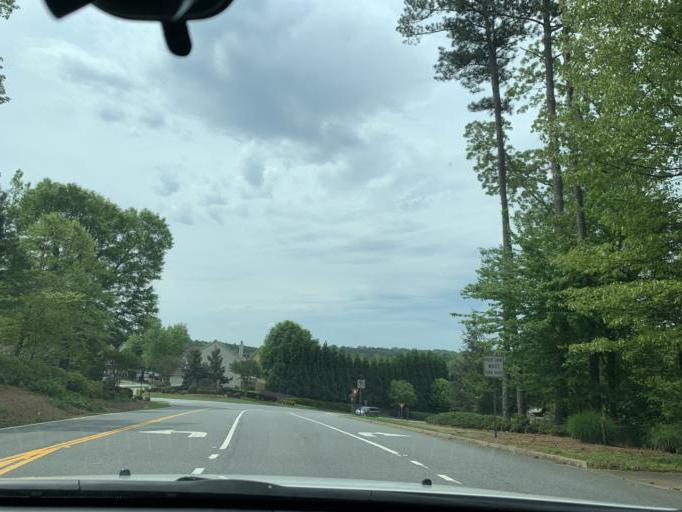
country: US
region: Georgia
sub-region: Forsyth County
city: Cumming
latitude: 34.1281
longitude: -84.1976
